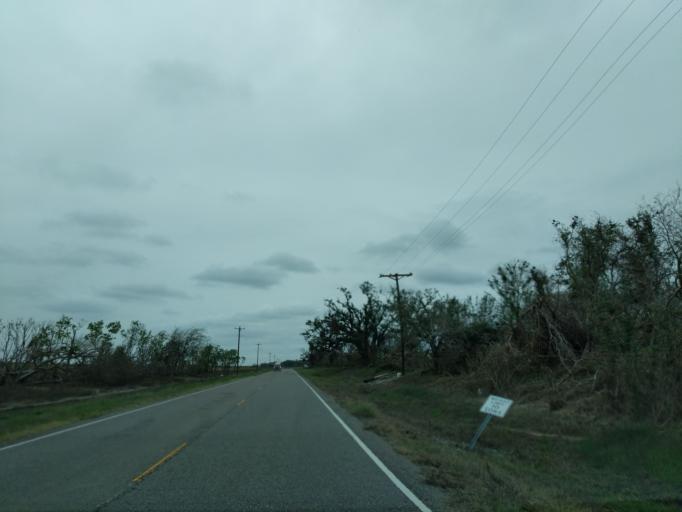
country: US
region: Louisiana
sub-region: Cameron Parish
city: Cameron
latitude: 29.7863
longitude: -93.1773
